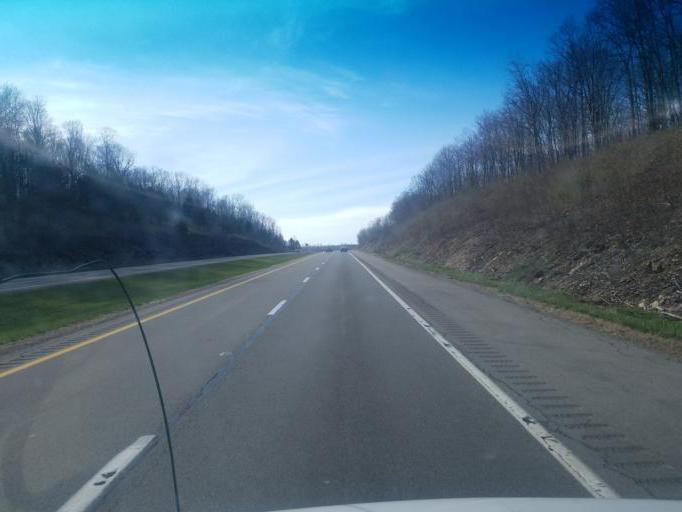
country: US
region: Ohio
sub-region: Logan County
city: Bellefontaine
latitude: 40.3345
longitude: -83.6853
